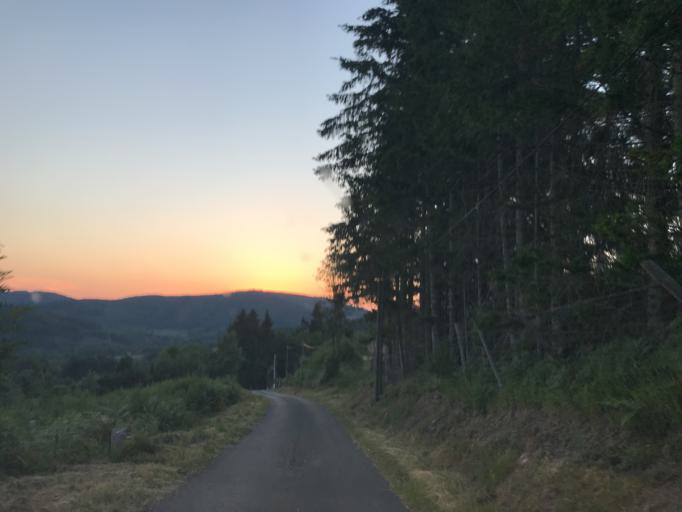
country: FR
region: Rhone-Alpes
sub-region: Departement de la Loire
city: Noiretable
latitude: 45.7866
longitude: 3.6894
